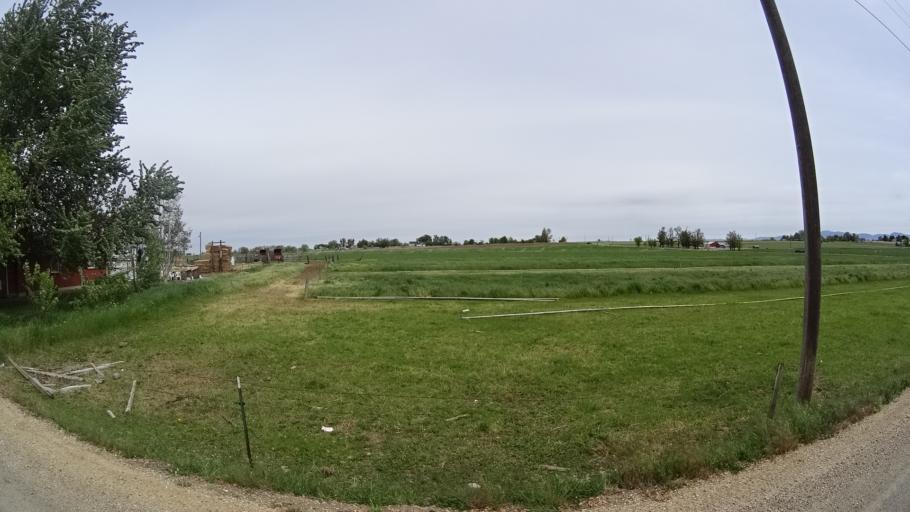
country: US
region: Idaho
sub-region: Ada County
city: Kuna
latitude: 43.5612
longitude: -116.4561
